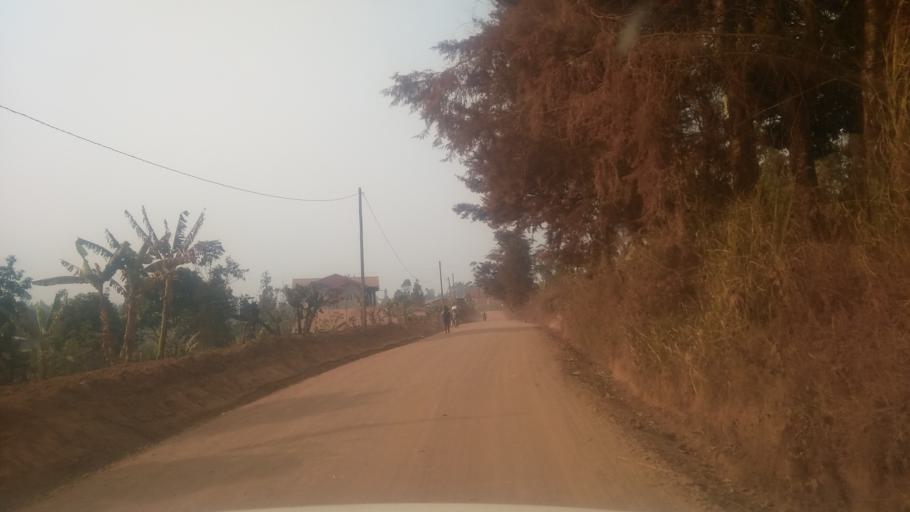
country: CM
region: West
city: Dschang
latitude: 5.4823
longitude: 10.1064
